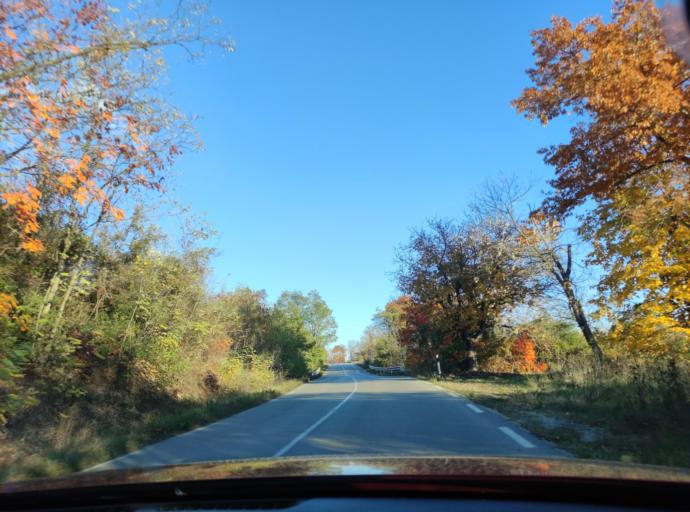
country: BG
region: Montana
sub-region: Obshtina Montana
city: Montana
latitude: 43.3980
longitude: 23.1039
